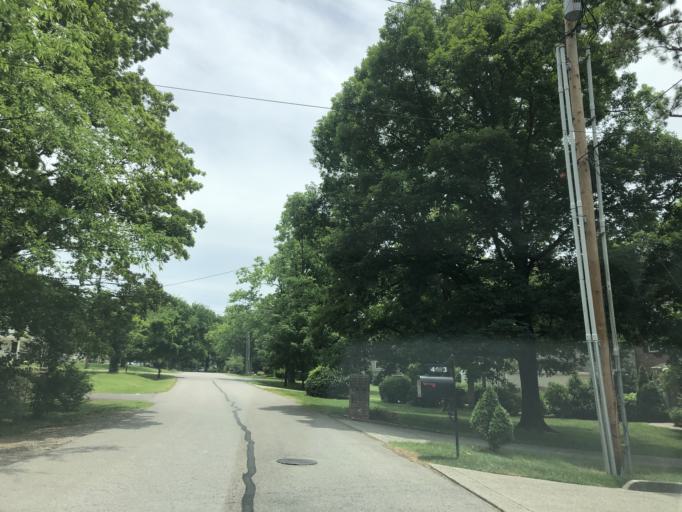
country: US
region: Tennessee
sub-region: Davidson County
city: Oak Hill
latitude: 36.0993
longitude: -86.7872
